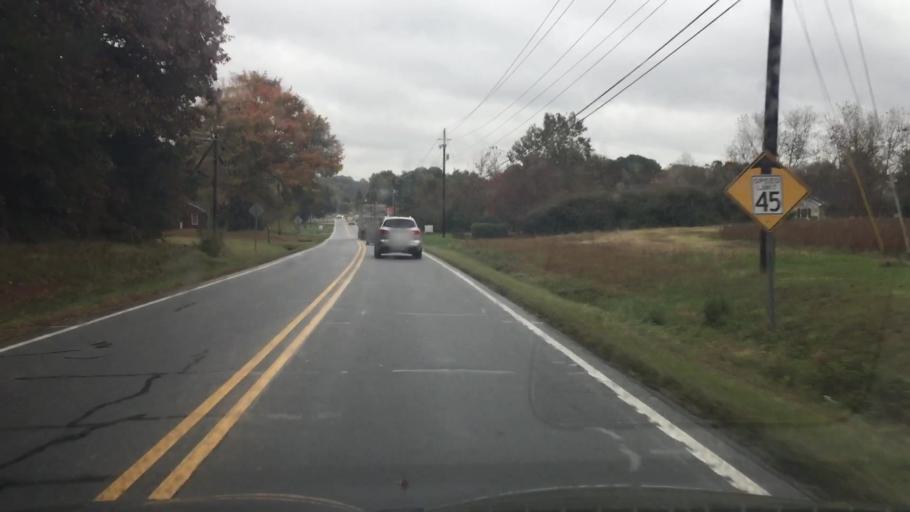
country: US
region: North Carolina
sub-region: Rowan County
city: Salisbury
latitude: 35.6638
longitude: -80.5194
